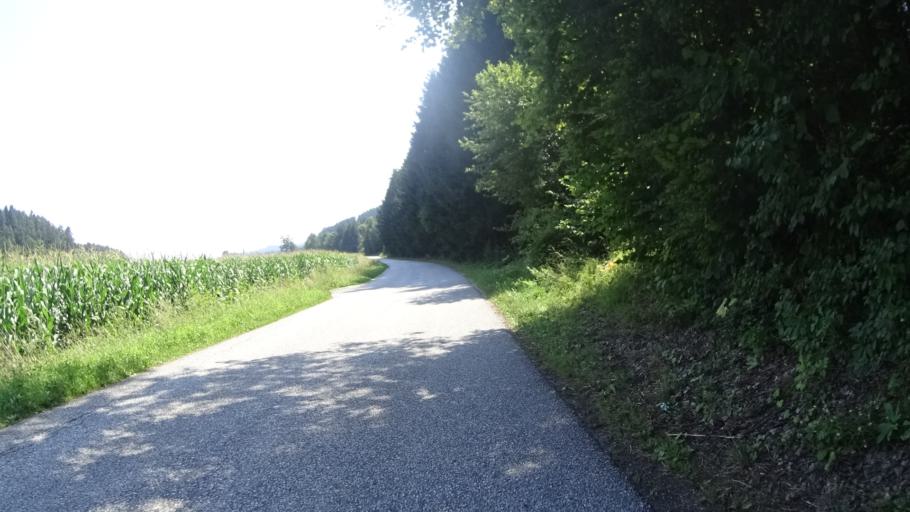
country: AT
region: Carinthia
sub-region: Politischer Bezirk Volkermarkt
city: Globasnitz
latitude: 46.5595
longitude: 14.6865
